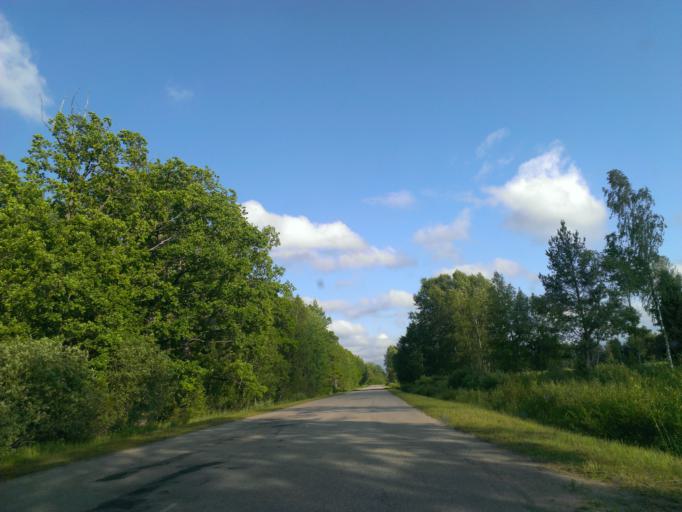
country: LV
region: Aizpute
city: Aizpute
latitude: 56.7916
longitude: 21.5085
